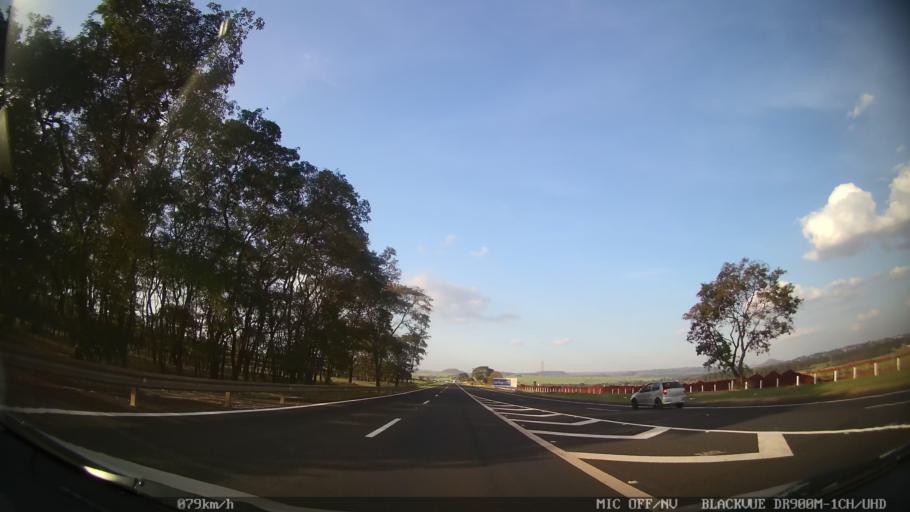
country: BR
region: Sao Paulo
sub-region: Ribeirao Preto
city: Ribeirao Preto
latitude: -21.1124
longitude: -47.7776
